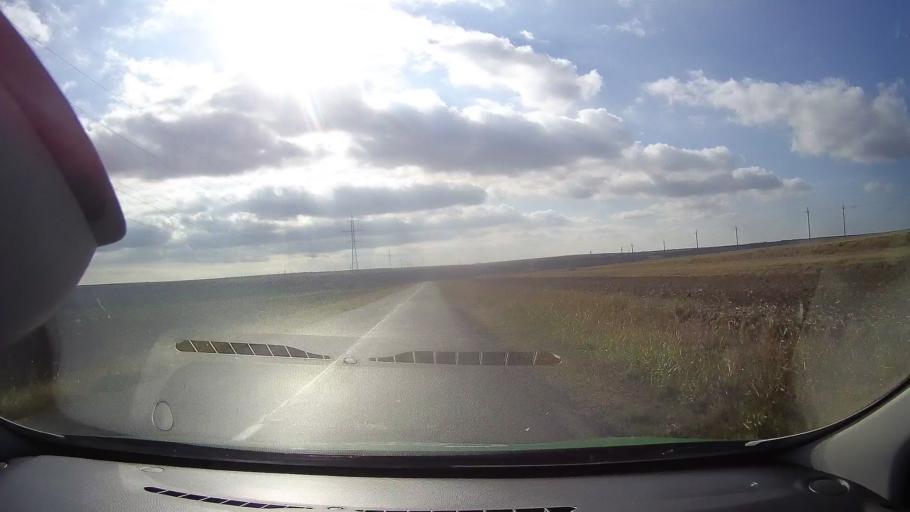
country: RO
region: Constanta
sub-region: Comuna Sacele
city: Sacele
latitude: 44.5031
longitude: 28.6633
